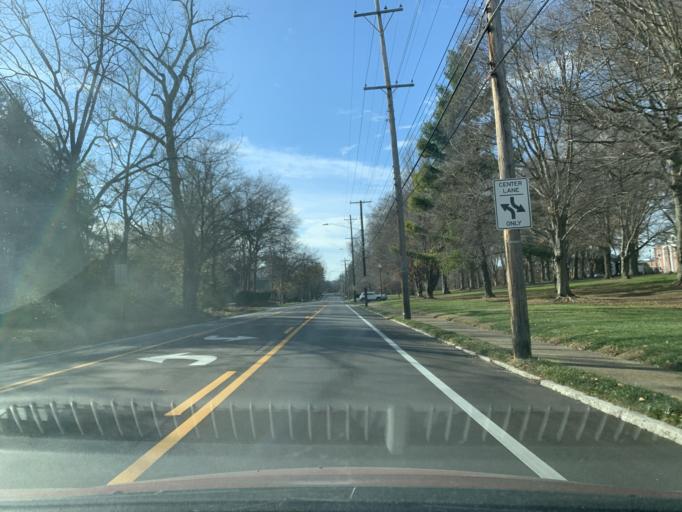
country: US
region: Kentucky
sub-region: Jefferson County
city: Saint Matthews
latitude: 38.2474
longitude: -85.6837
